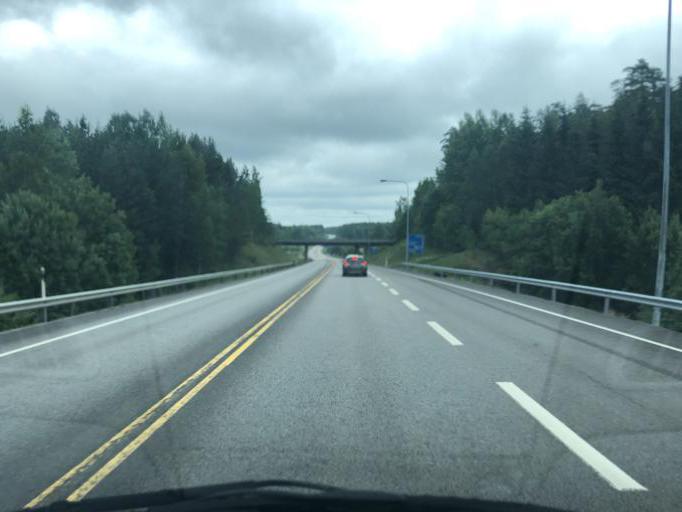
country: FI
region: Uusimaa
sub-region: Loviisa
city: Perna
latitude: 60.4952
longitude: 25.9615
